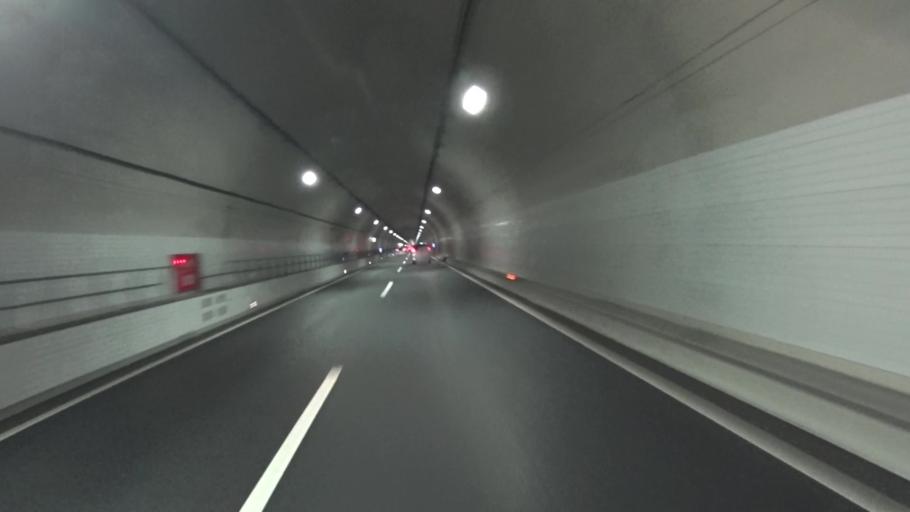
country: JP
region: Kyoto
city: Muko
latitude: 34.9321
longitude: 135.6658
